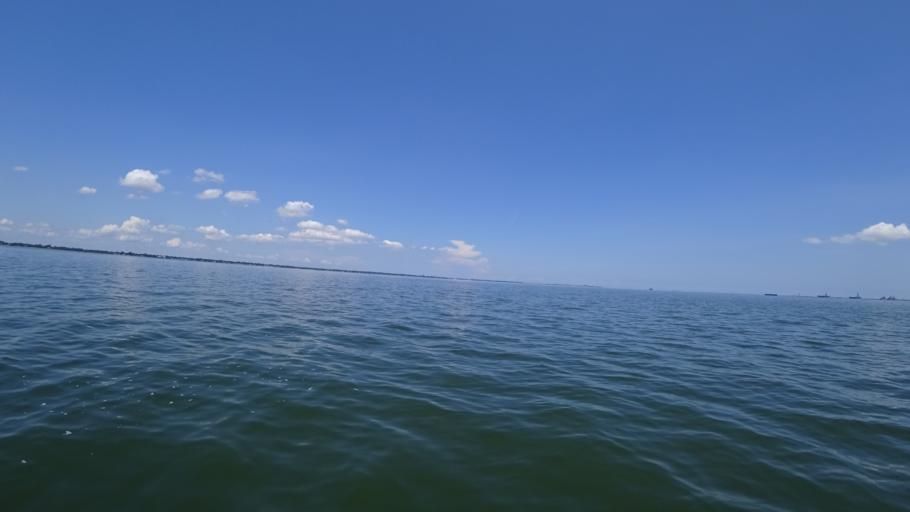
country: US
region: Virginia
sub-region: City of Newport News
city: Newport News
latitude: 36.9549
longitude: -76.3849
